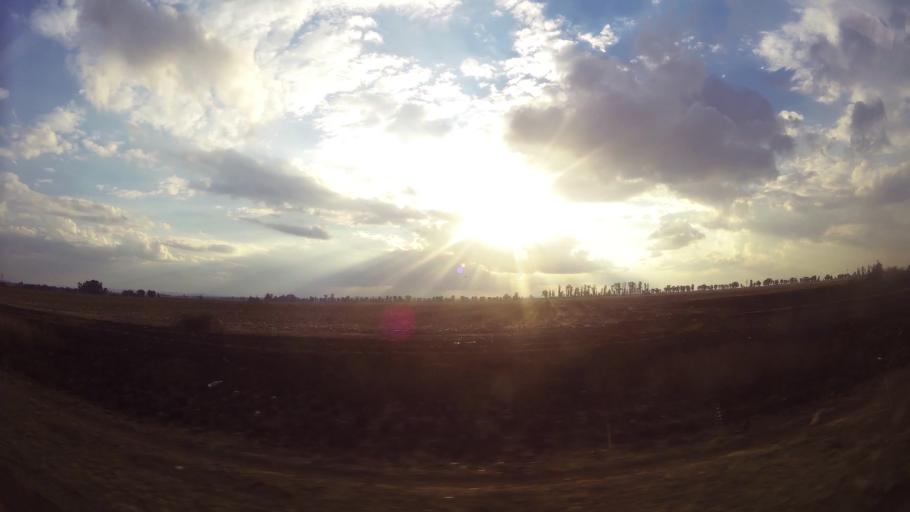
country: ZA
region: Gauteng
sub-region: Sedibeng District Municipality
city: Vanderbijlpark
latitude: -26.6570
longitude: 27.8015
